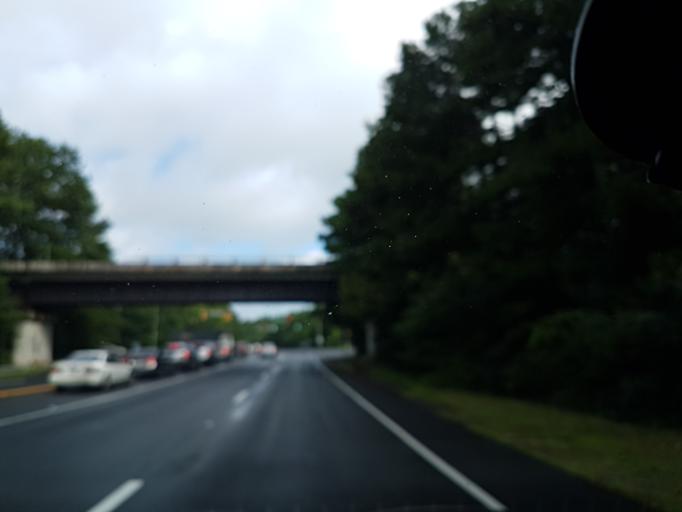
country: US
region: Georgia
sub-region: Fulton County
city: Fairburn
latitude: 33.5737
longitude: -84.5658
